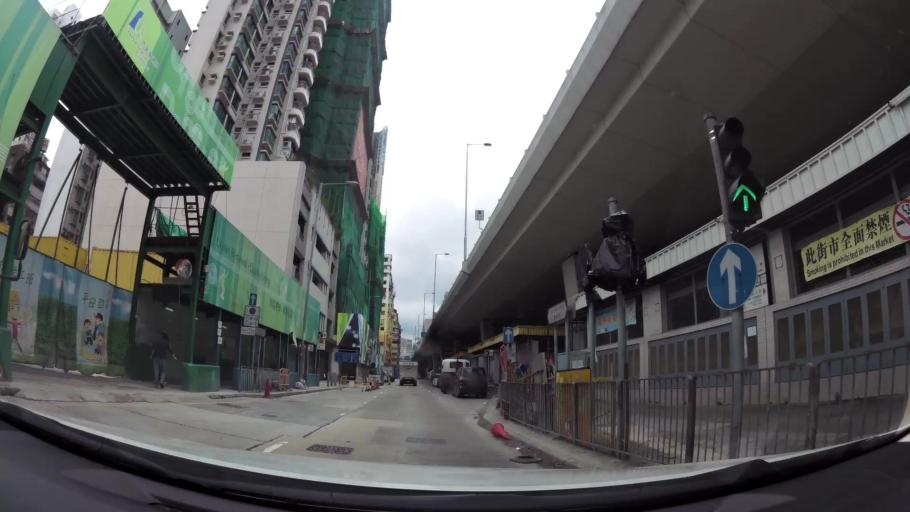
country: HK
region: Sham Shui Po
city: Sham Shui Po
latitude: 22.3270
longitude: 114.1597
